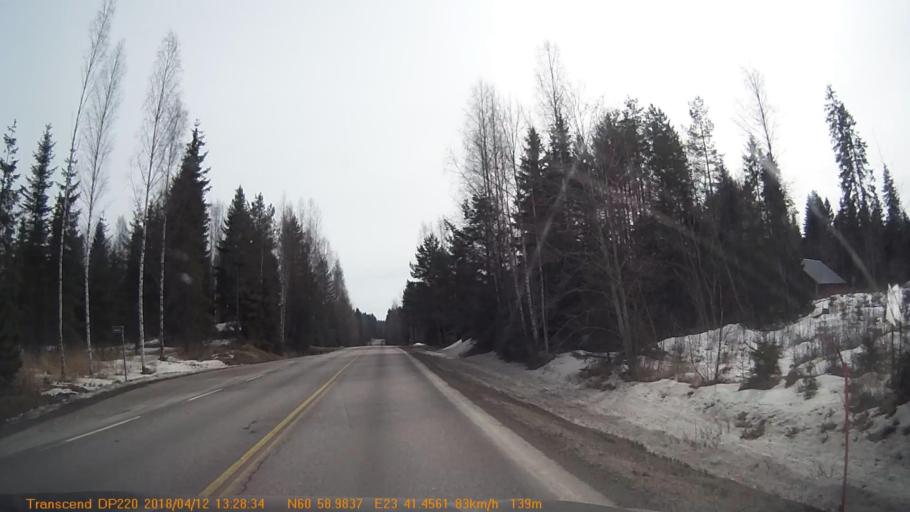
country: FI
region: Pirkanmaa
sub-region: Etelae-Pirkanmaa
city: Kylmaekoski
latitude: 60.9828
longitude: 23.6912
